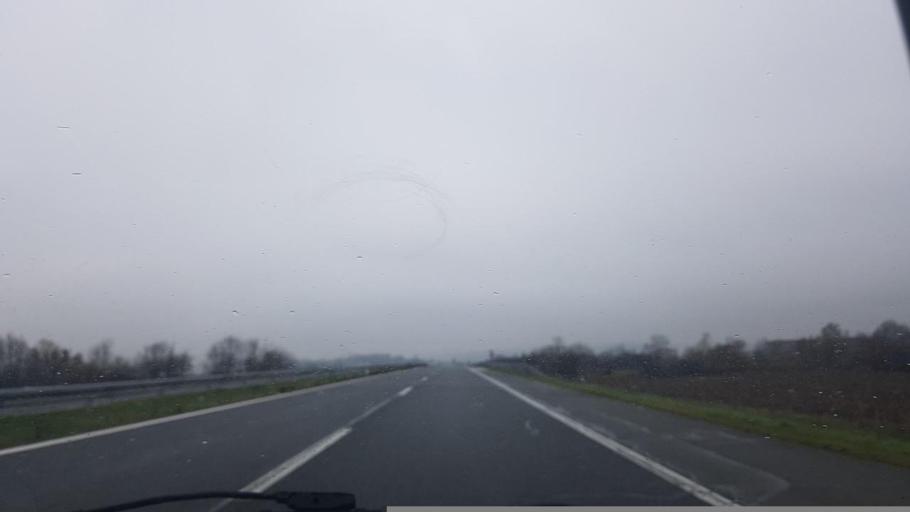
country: HR
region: Krapinsko-Zagorska
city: Oroslavje
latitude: 46.0118
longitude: 15.8898
